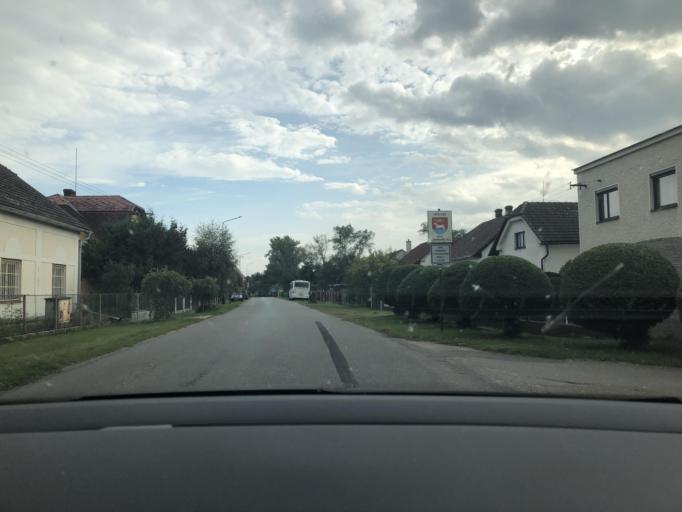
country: CZ
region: Pardubicky
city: Recany nad Labem
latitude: 50.0625
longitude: 15.4832
